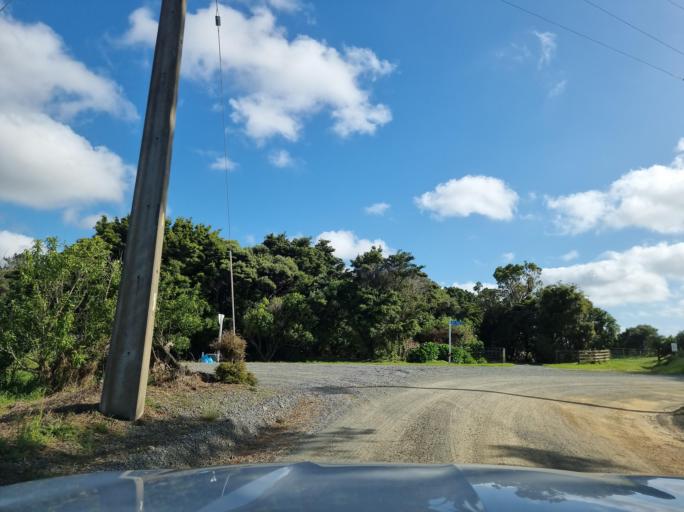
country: NZ
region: Auckland
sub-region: Auckland
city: Wellsford
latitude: -36.1273
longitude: 174.5941
